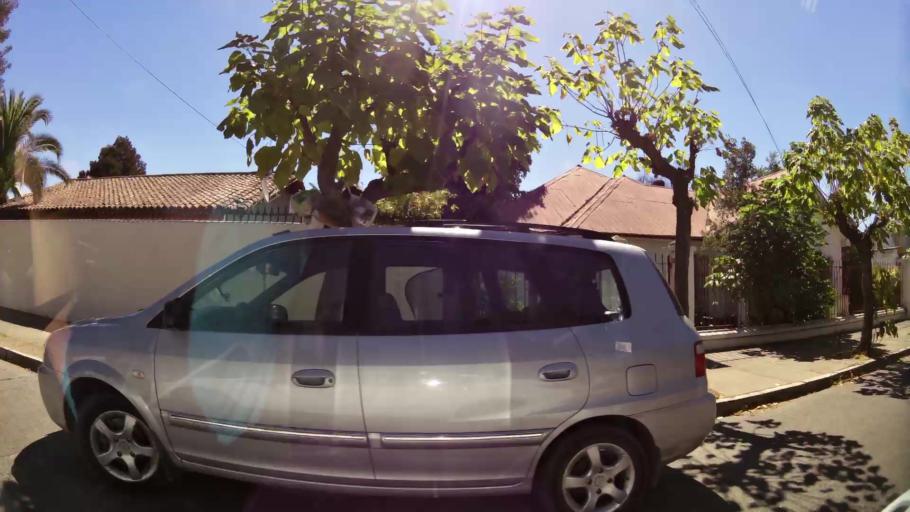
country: CL
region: O'Higgins
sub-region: Provincia de Colchagua
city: Chimbarongo
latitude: -34.5830
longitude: -70.9927
